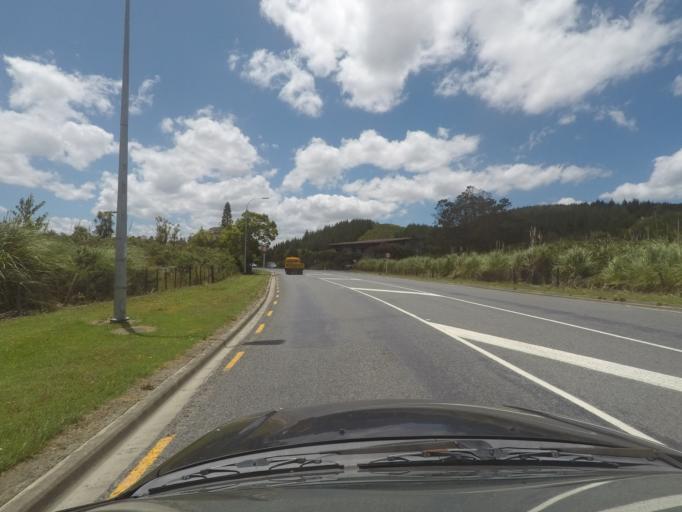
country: NZ
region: Northland
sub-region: Whangarei
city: Whangarei
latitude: -35.7514
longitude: 174.3202
